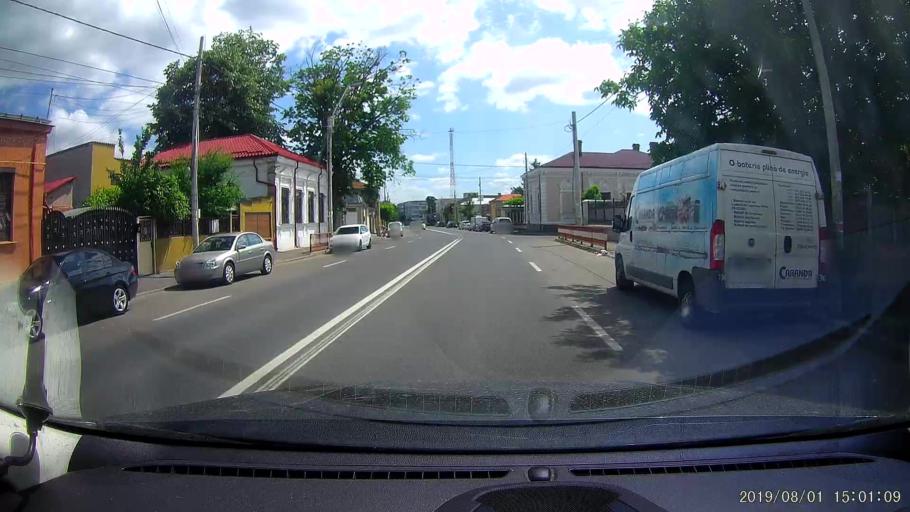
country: RO
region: Braila
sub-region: Municipiul Braila
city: Braila
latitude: 45.2740
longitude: 27.9608
